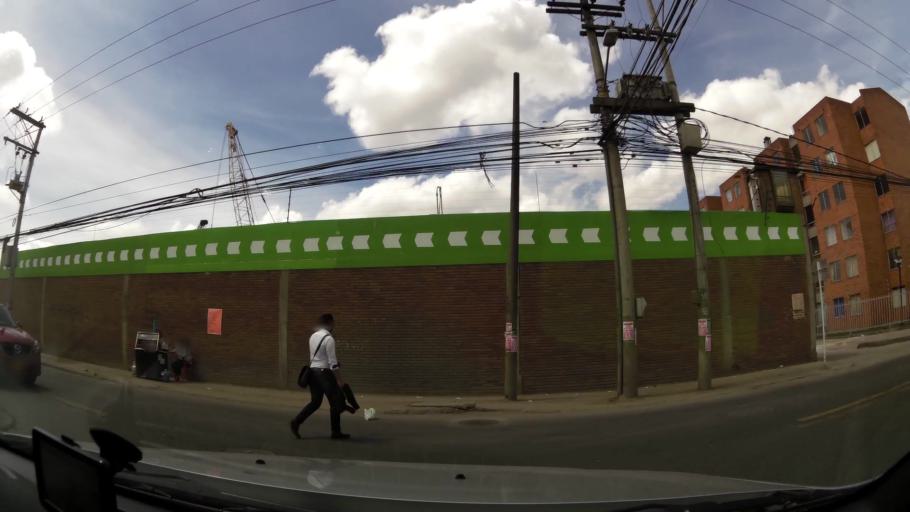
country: CO
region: Bogota D.C.
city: Bogota
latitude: 4.6534
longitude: -74.1408
